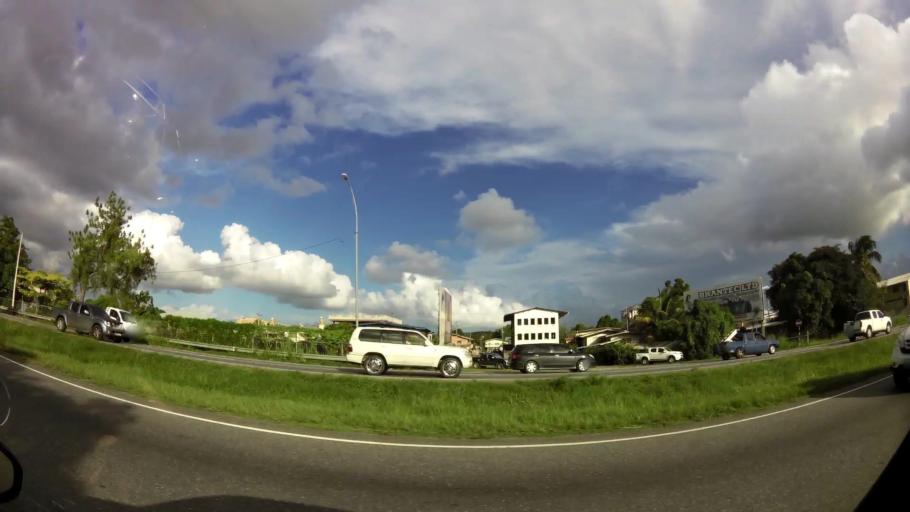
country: TT
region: Chaguanas
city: Chaguanas
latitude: 10.5132
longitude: -61.4077
